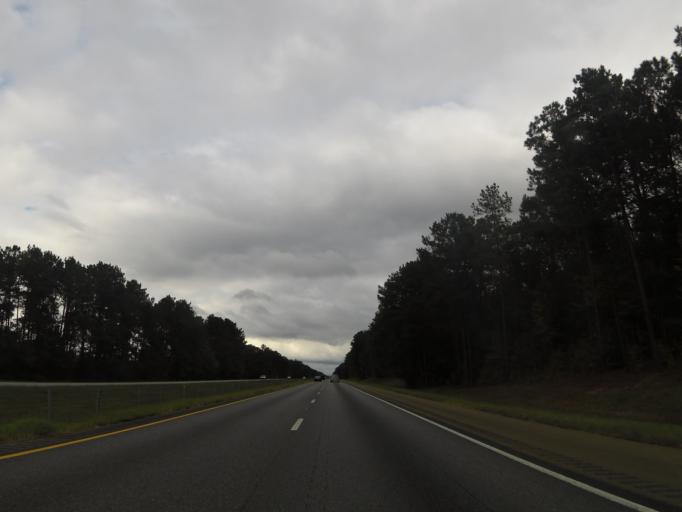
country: US
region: Alabama
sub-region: Butler County
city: Georgiana
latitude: 31.6685
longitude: -86.7611
